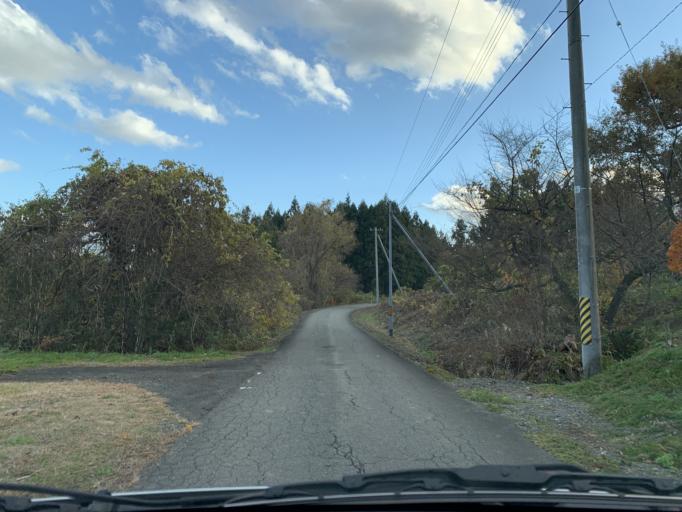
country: JP
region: Iwate
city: Mizusawa
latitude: 39.1092
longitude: 141.0392
